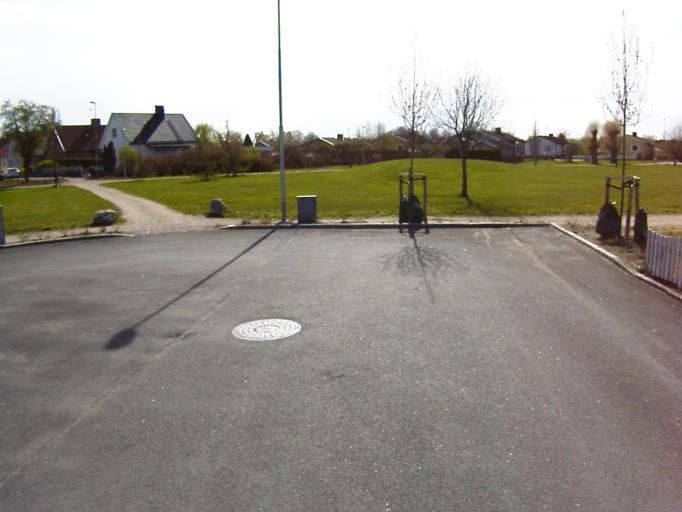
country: SE
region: Skane
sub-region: Kristianstads Kommun
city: Kristianstad
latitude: 56.0544
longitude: 14.1545
